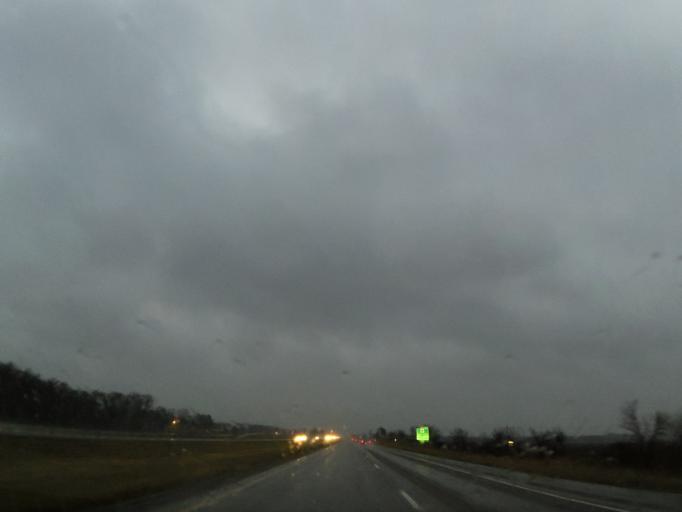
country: US
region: Iowa
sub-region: Worth County
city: Northwood
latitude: 43.4227
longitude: -93.3494
